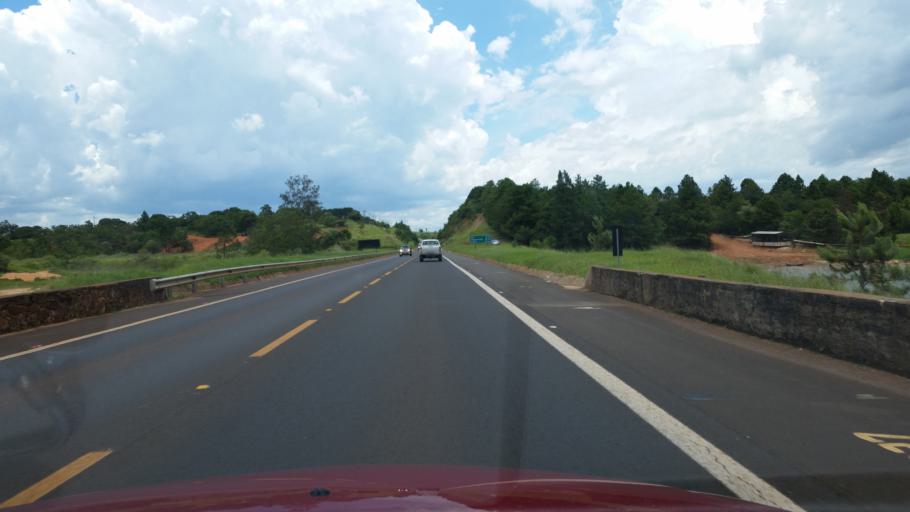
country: BR
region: Sao Paulo
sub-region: Itai
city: Itai
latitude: -23.2728
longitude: -49.0159
